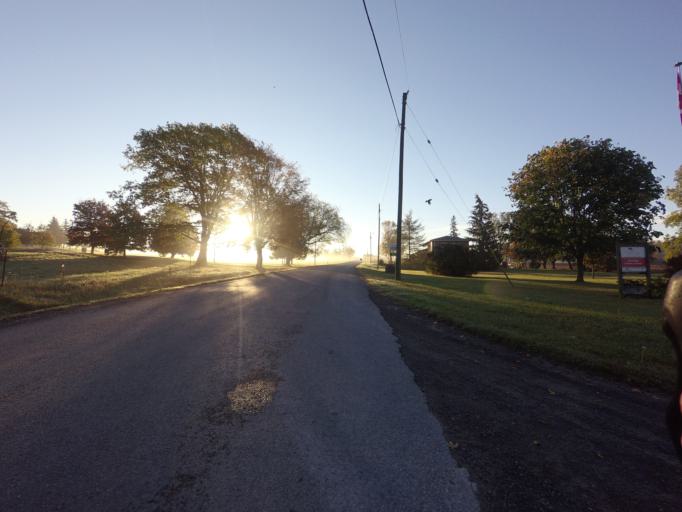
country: CA
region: Ontario
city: Quinte West
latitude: 44.0312
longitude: -77.5676
